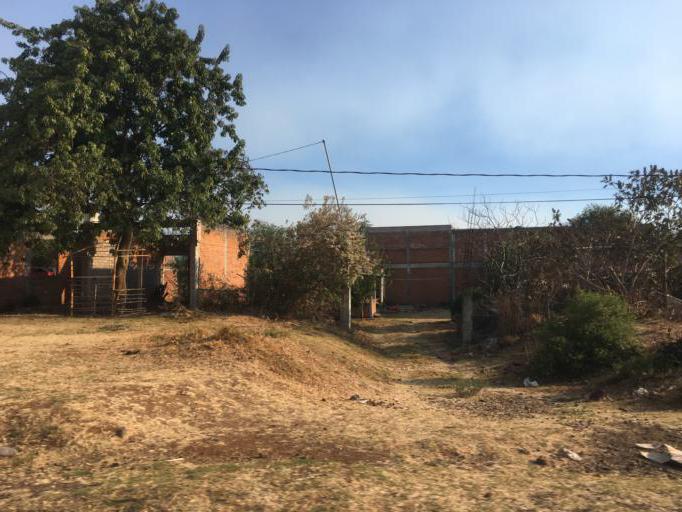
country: MX
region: Michoacan
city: Santa Fe de la Laguna
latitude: 19.6700
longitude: -101.5529
